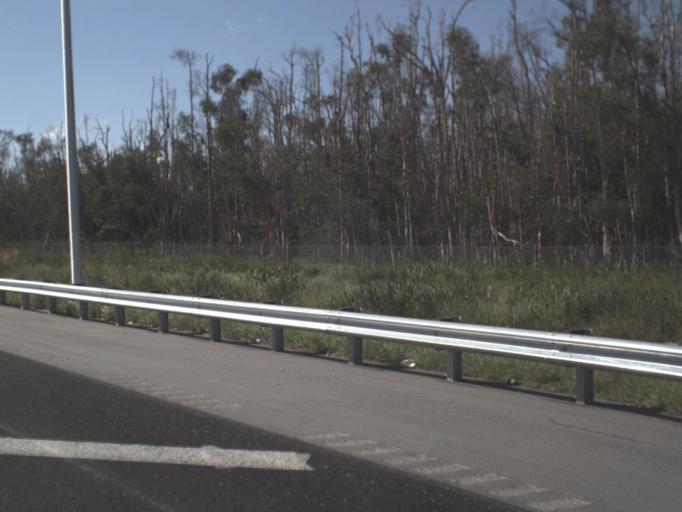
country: US
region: Florida
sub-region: Miami-Dade County
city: Doral
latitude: 25.8614
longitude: -80.3879
